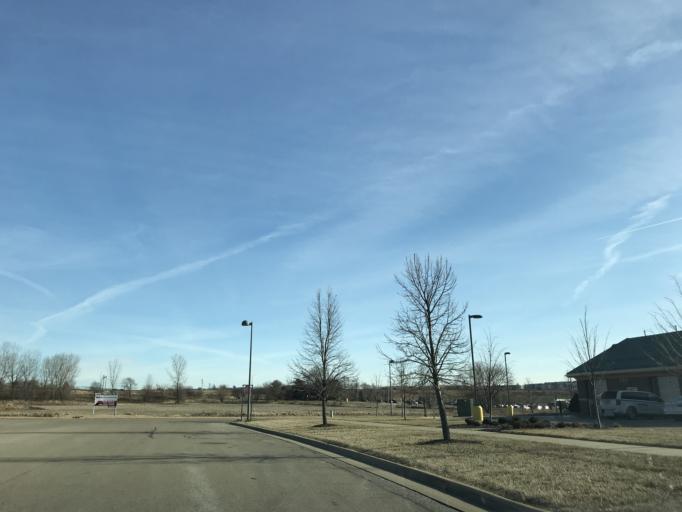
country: US
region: Wisconsin
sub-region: Dane County
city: Sun Prairie
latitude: 43.1500
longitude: -89.2888
